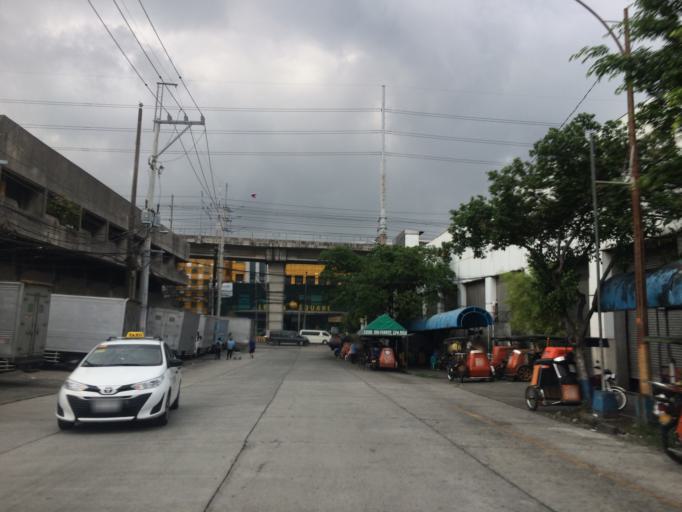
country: PH
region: Calabarzon
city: Bagong Pagasa
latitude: 14.6586
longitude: 121.0175
